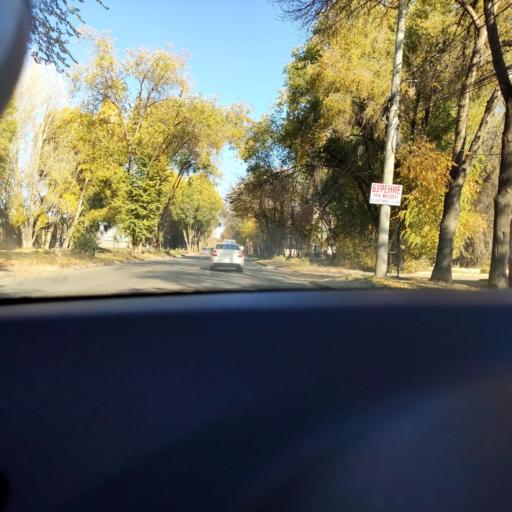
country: RU
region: Samara
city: Petra-Dubrava
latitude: 53.2299
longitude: 50.2914
